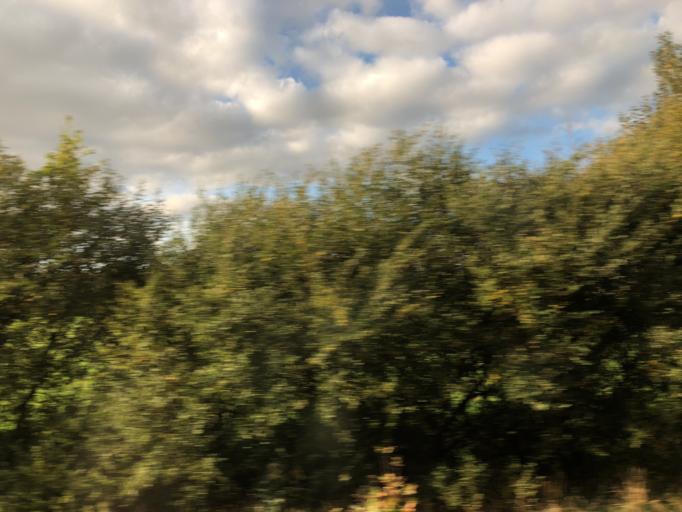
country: DE
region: Schleswig-Holstein
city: Padenstedt
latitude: 54.0372
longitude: 9.9154
